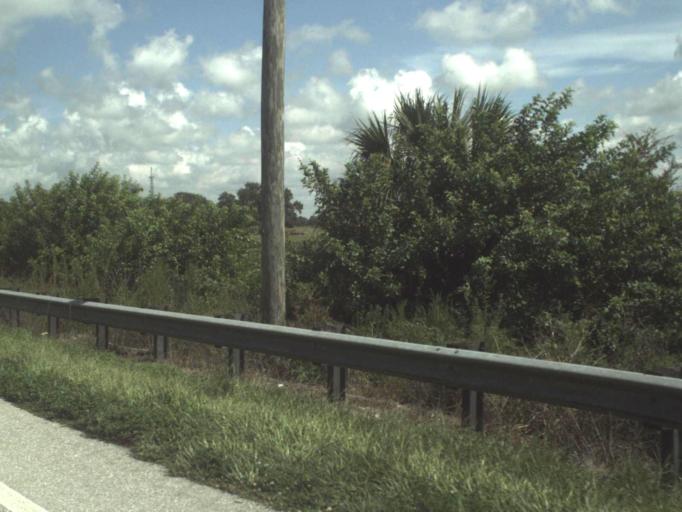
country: US
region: Florida
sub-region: Martin County
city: Indiantown
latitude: 27.0807
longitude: -80.5591
